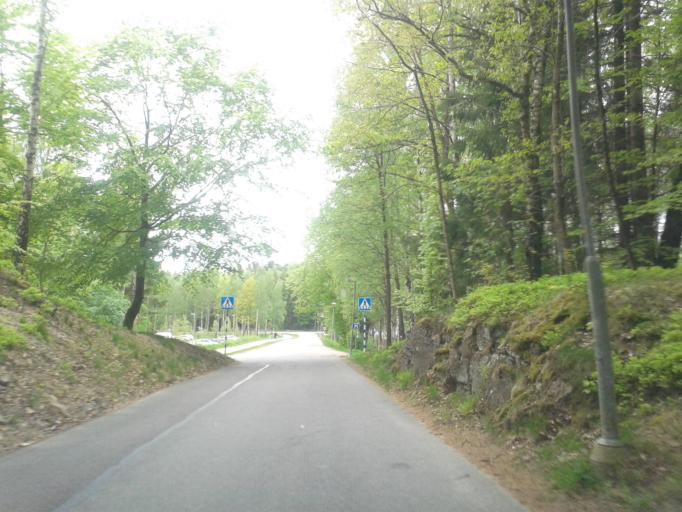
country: SE
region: Vaestra Goetaland
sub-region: Kungalvs Kommun
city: Kungalv
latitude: 57.8720
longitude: 12.0003
